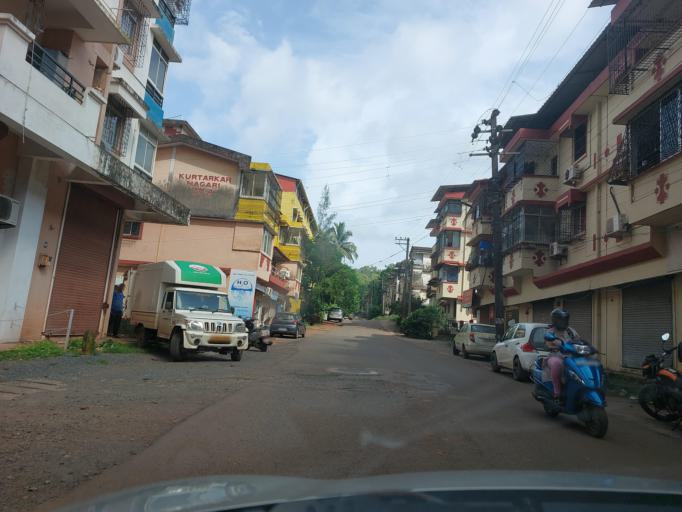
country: IN
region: Goa
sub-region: North Goa
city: Ponda
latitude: 15.3974
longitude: 74.0073
